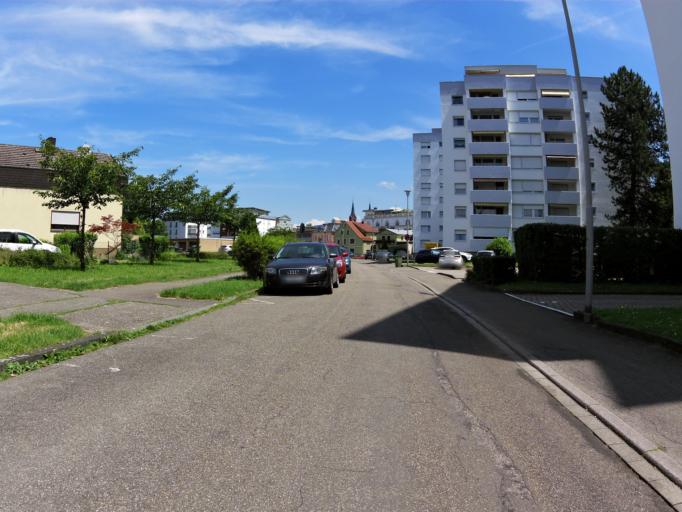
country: DE
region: Baden-Wuerttemberg
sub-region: Freiburg Region
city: Lahr
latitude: 48.3361
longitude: 7.8653
